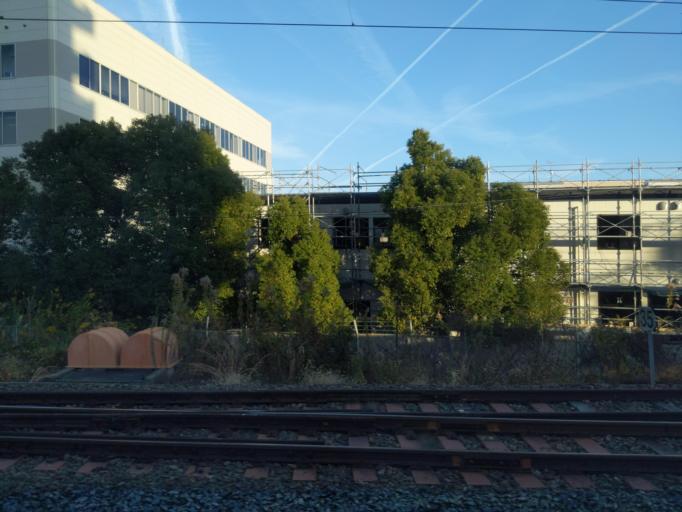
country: JP
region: Aichi
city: Nagoya-shi
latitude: 35.1865
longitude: 136.9372
